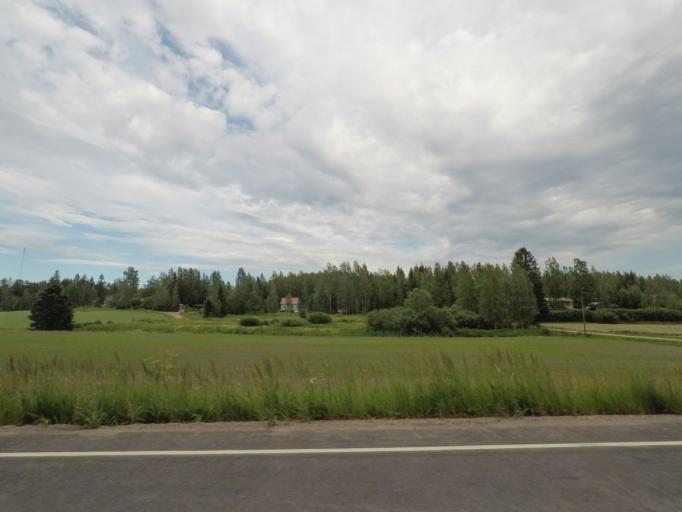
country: FI
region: Uusimaa
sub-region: Porvoo
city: Pukkila
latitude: 60.7762
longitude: 25.4540
